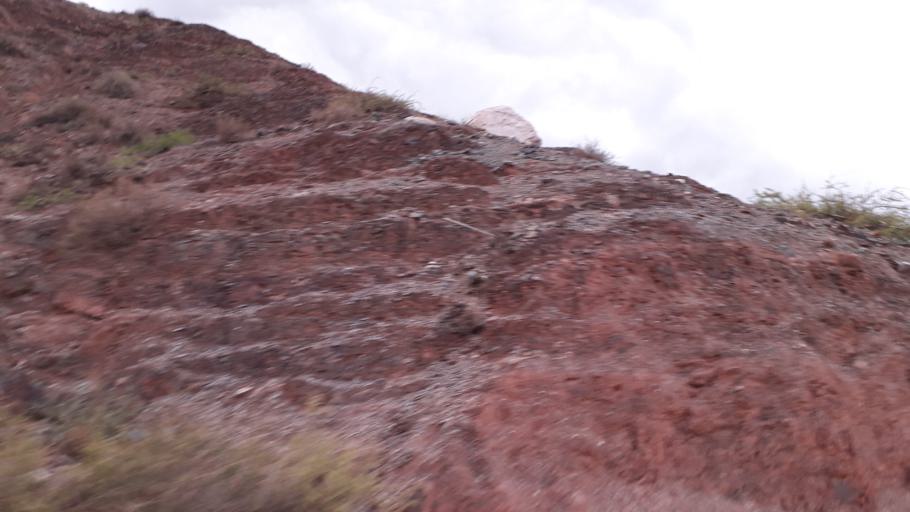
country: AR
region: Jujuy
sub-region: Departamento de Tumbaya
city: Tumbaya
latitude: -23.7462
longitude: -65.5076
